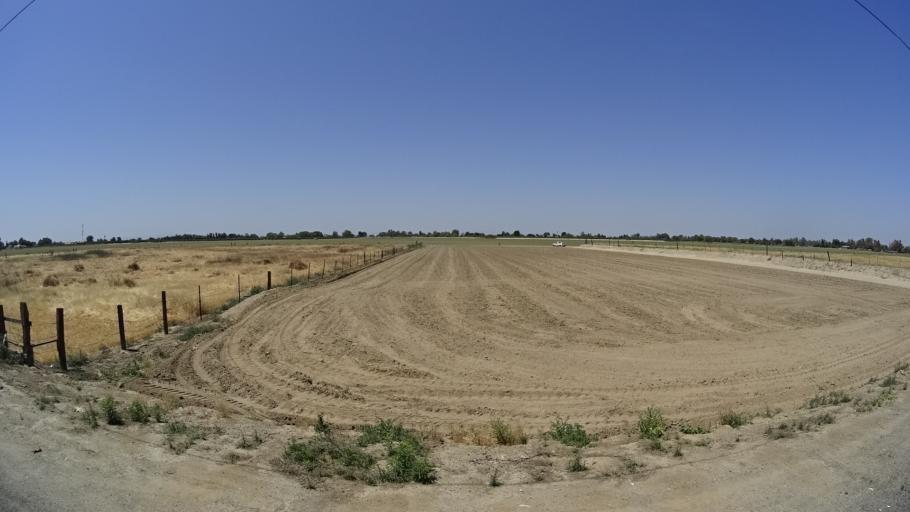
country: US
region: California
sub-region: Kings County
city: Lemoore
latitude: 36.2761
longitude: -119.7630
